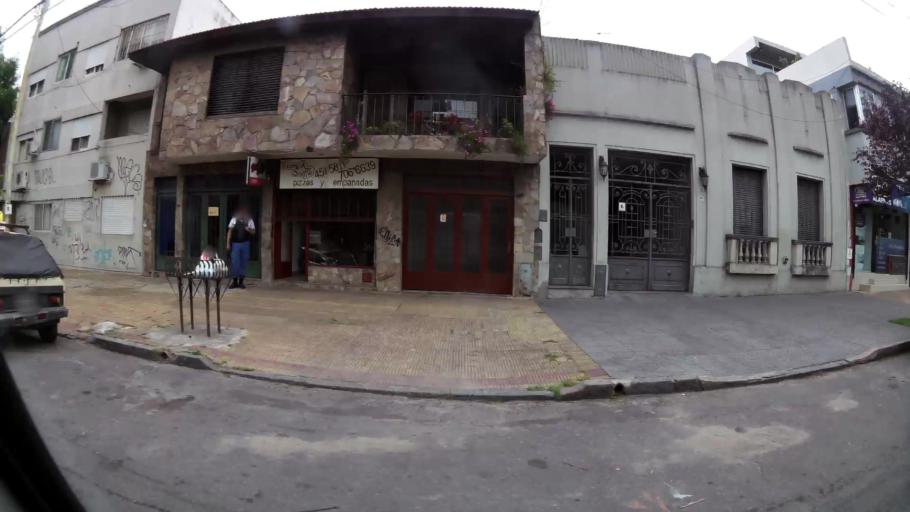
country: AR
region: Buenos Aires
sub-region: Partido de La Plata
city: La Plata
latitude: -34.9285
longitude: -57.9500
